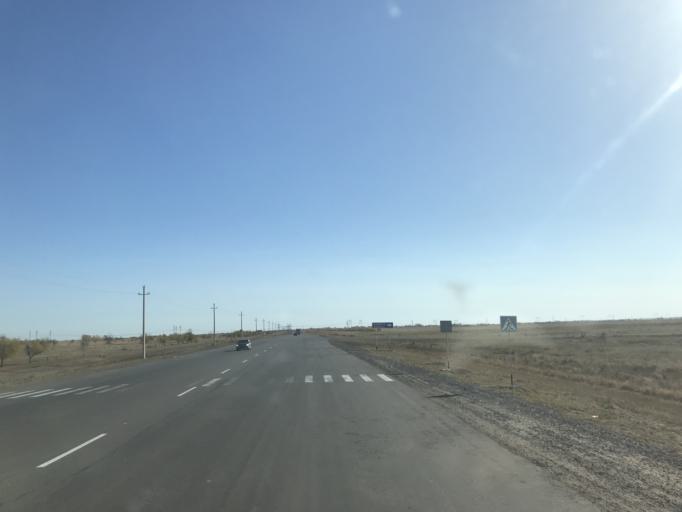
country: KZ
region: Pavlodar
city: Pavlodar
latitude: 52.1453
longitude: 77.0674
